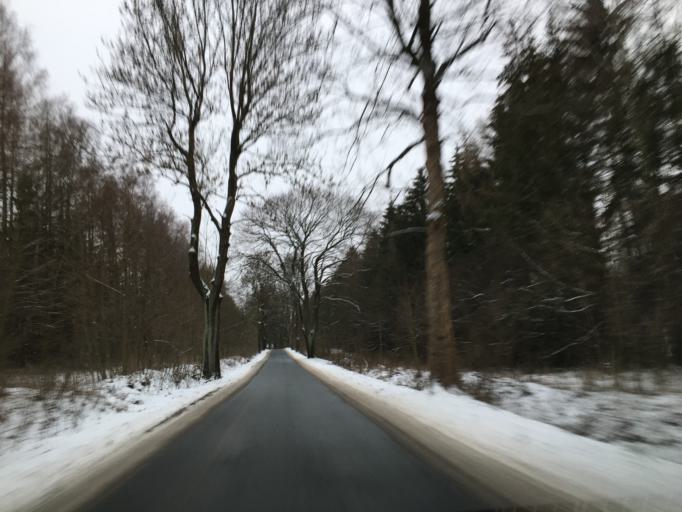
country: PL
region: Lower Silesian Voivodeship
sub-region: Powiat kamiennogorski
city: Lubawka
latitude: 50.6503
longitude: 16.0575
